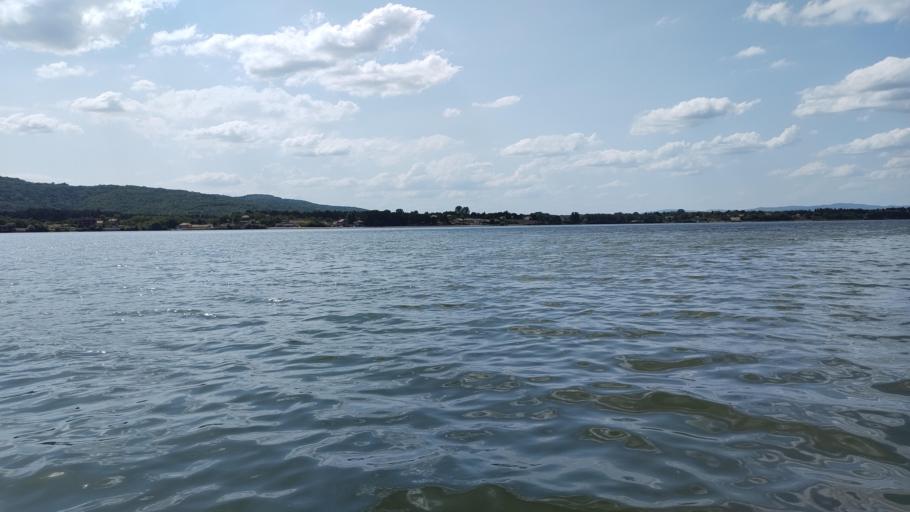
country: RS
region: Central Serbia
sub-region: Branicevski Okrug
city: Golubac
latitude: 44.6760
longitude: 21.6177
